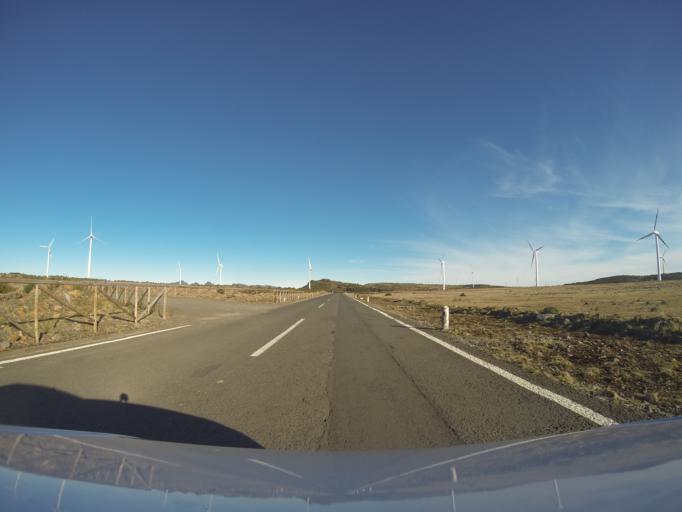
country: PT
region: Madeira
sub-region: Sao Vicente
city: Sao Vicente
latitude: 32.7610
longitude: -17.0661
